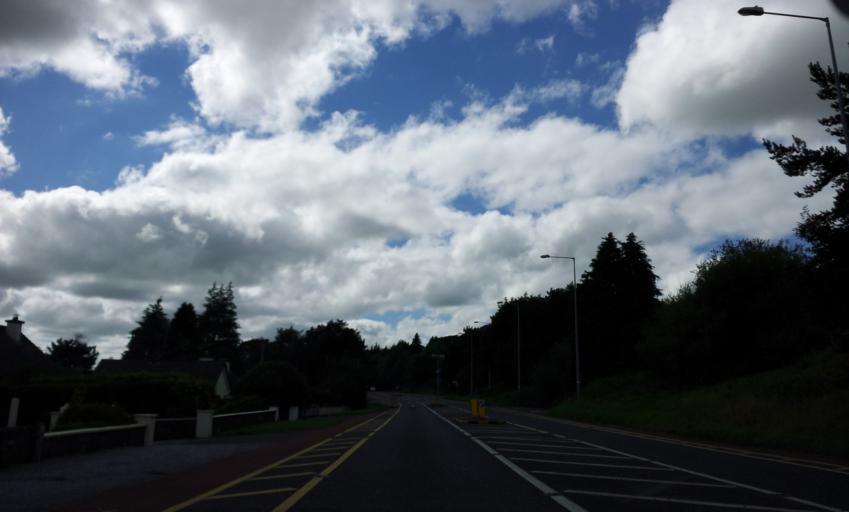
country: IE
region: Munster
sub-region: County Cork
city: Killumney
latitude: 51.8723
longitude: -8.7295
